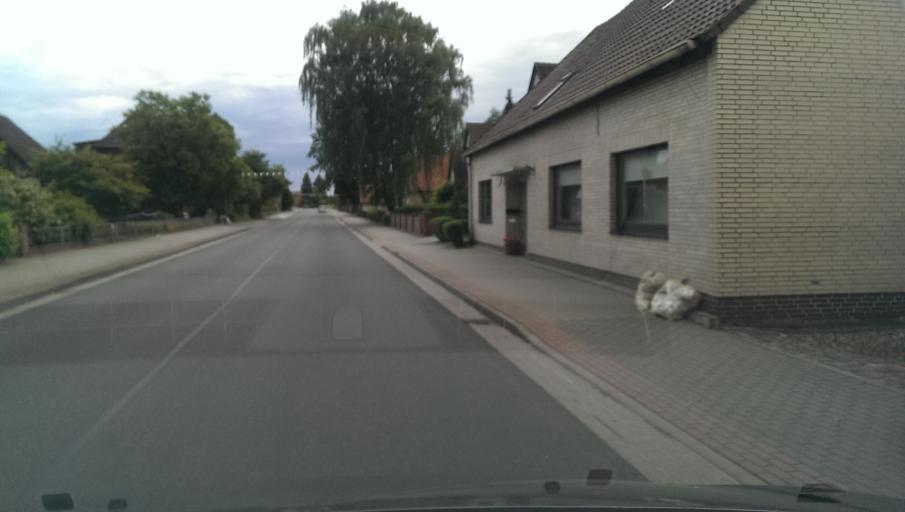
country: DE
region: Lower Saxony
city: Parsau
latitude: 52.5418
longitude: 10.8956
